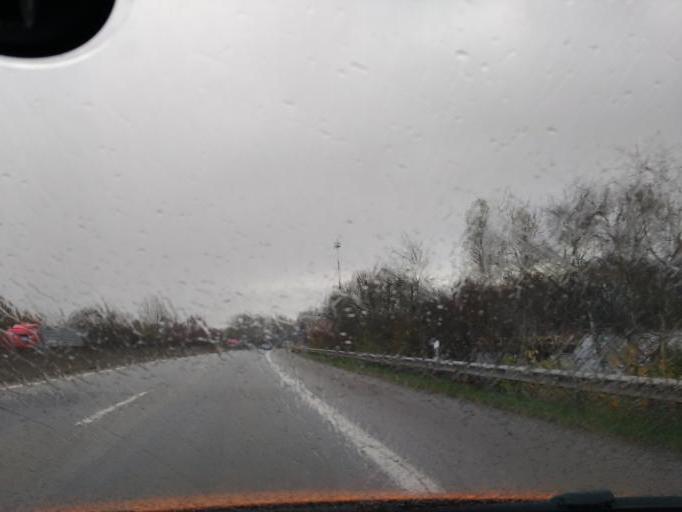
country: DE
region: Hamburg
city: Rothenburgsort
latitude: 53.5034
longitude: 10.0390
